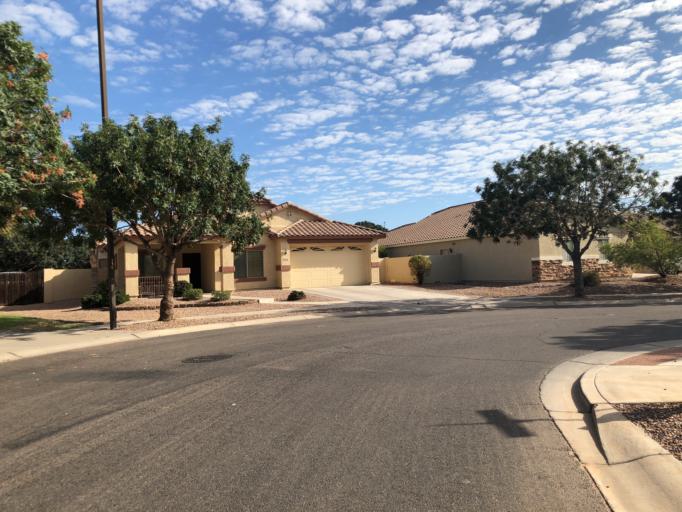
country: US
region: Arizona
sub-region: Maricopa County
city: Queen Creek
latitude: 33.2830
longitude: -111.7002
